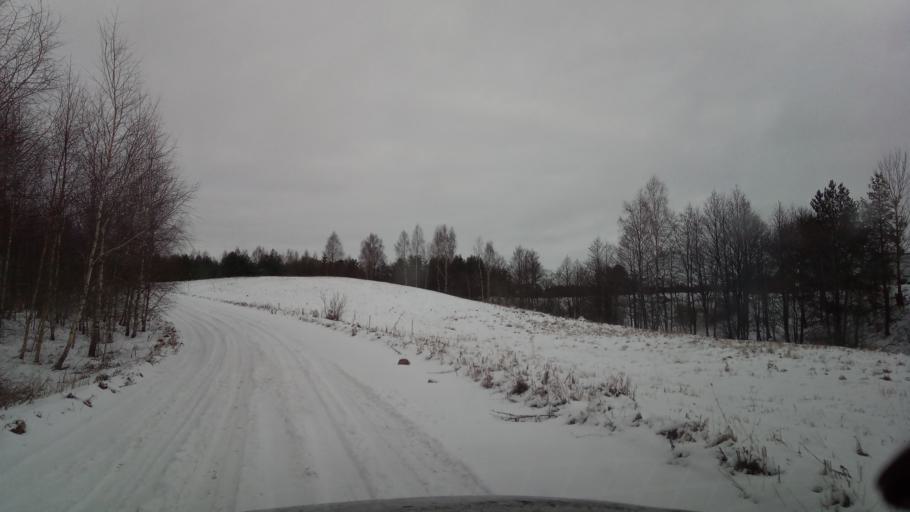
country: LT
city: Zarasai
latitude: 55.6832
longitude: 26.1062
